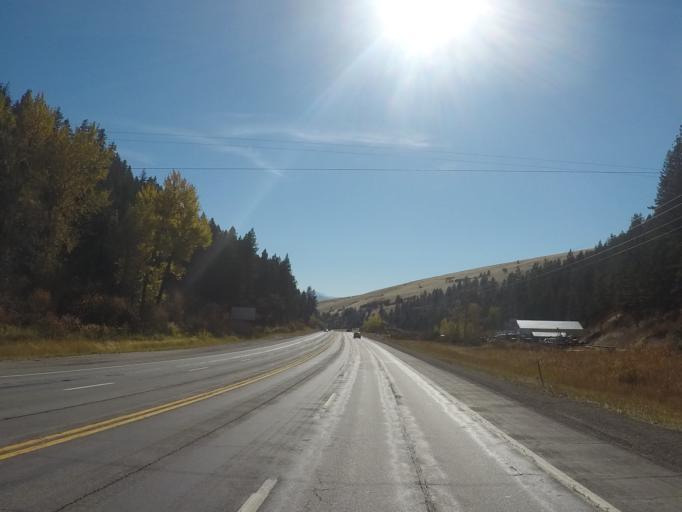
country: US
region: Montana
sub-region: Missoula County
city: Frenchtown
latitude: 47.0065
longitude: -114.1251
